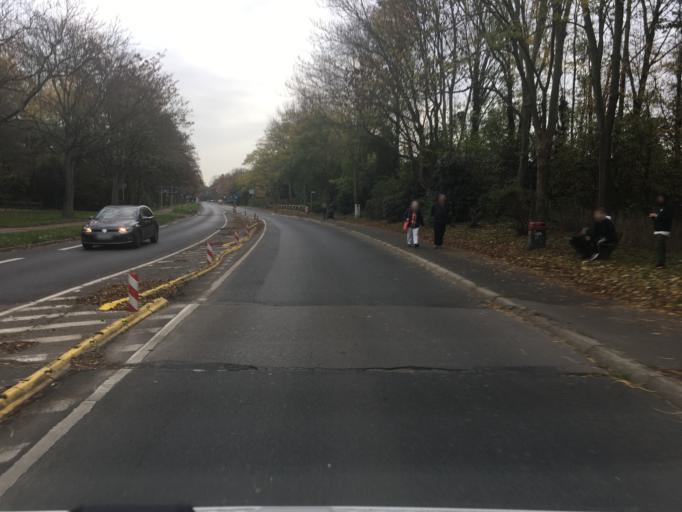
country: DE
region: North Rhine-Westphalia
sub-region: Regierungsbezirk Koln
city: Hurth
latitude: 50.8844
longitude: 6.8812
